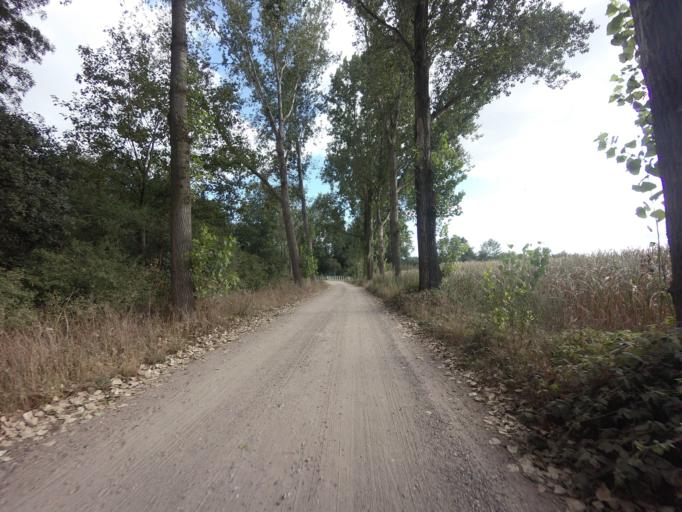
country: NL
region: North Brabant
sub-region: Gemeente Grave
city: Grave
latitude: 51.7371
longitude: 5.7406
